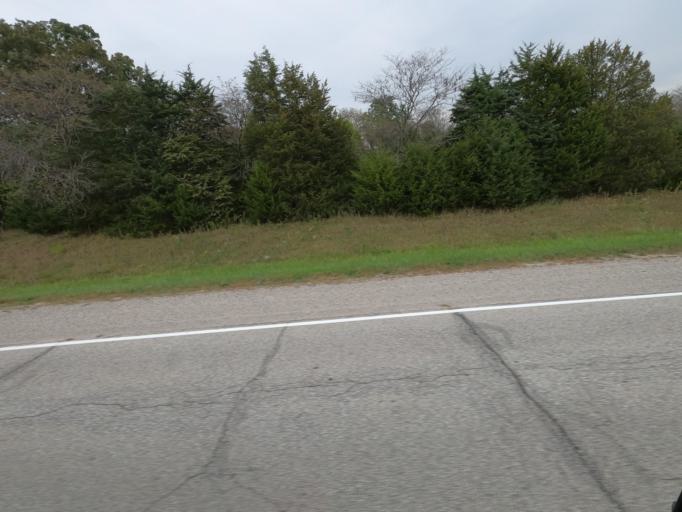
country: US
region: Iowa
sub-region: Van Buren County
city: Keosauqua
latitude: 40.8347
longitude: -91.9867
